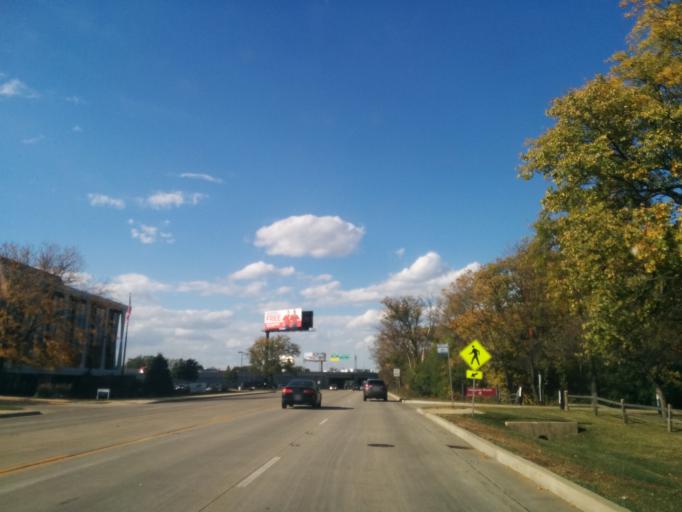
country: US
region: Illinois
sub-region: Cook County
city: Rosemont
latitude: 42.0055
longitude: -87.8664
